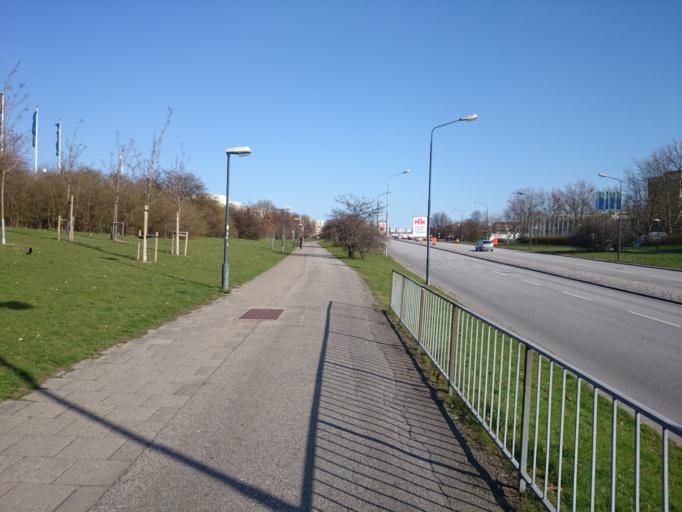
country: SE
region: Skane
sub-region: Malmo
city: Malmoe
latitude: 55.5900
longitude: 13.0319
